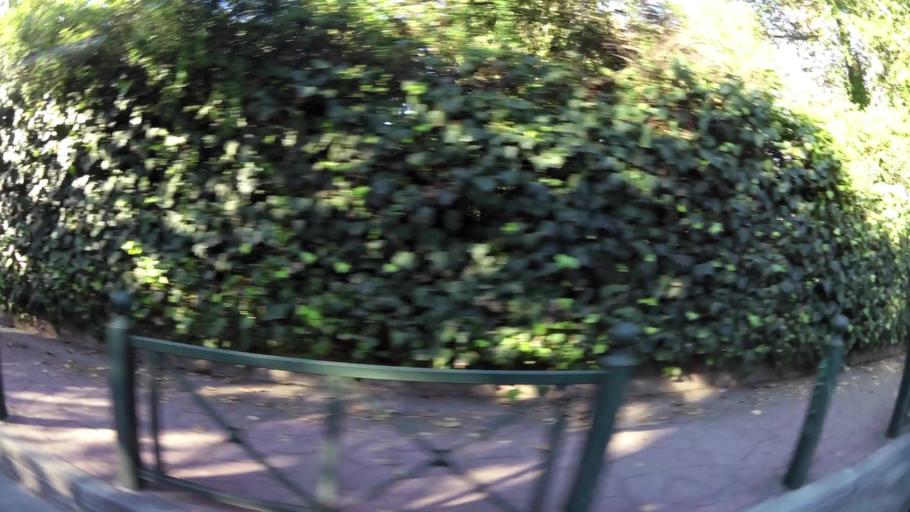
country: GR
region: Attica
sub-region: Nomarchia Athinas
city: Kifisia
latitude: 38.0739
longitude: 23.8061
